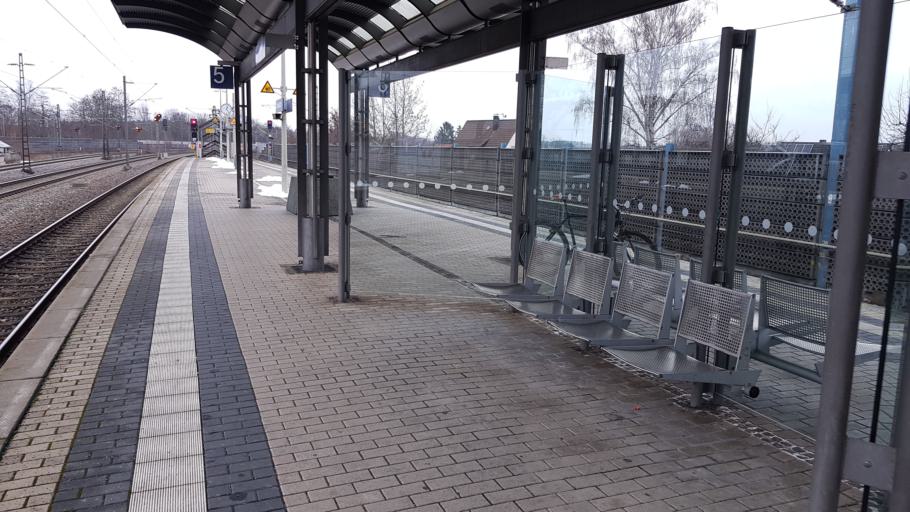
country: DE
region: Bavaria
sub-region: Regierungsbezirk Mittelfranken
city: Schwabach
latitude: 49.3265
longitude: 11.0356
